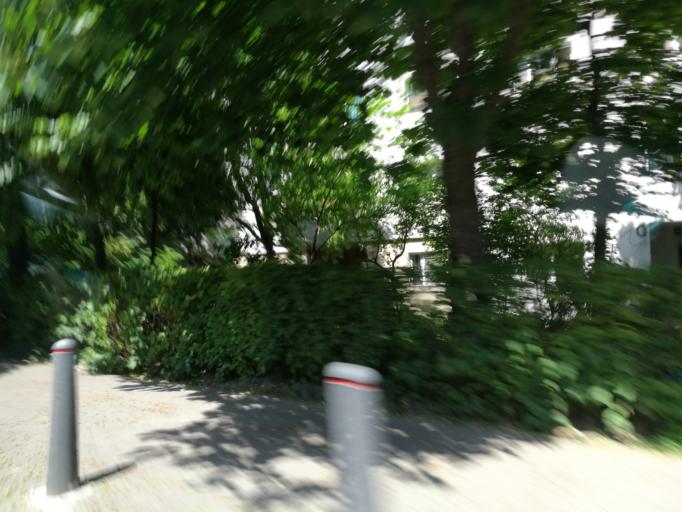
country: RO
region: Constanta
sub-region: Municipiul Constanta
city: Constanta
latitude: 44.2023
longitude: 28.6285
